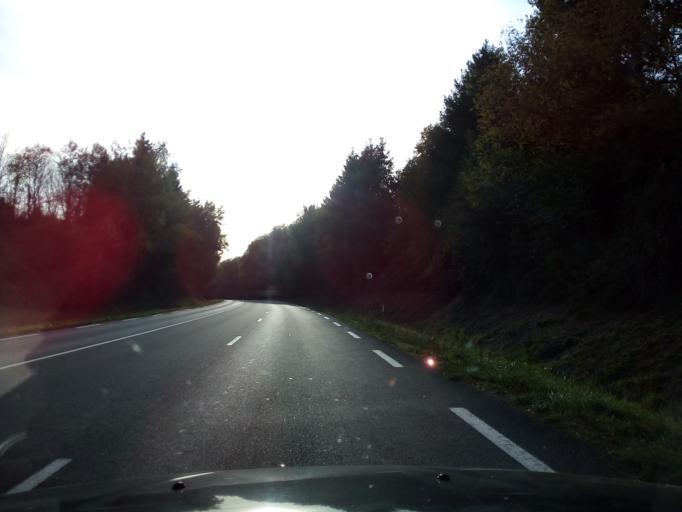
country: FR
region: Poitou-Charentes
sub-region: Departement de la Charente
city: Confolens
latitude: 46.0636
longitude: 0.6705
